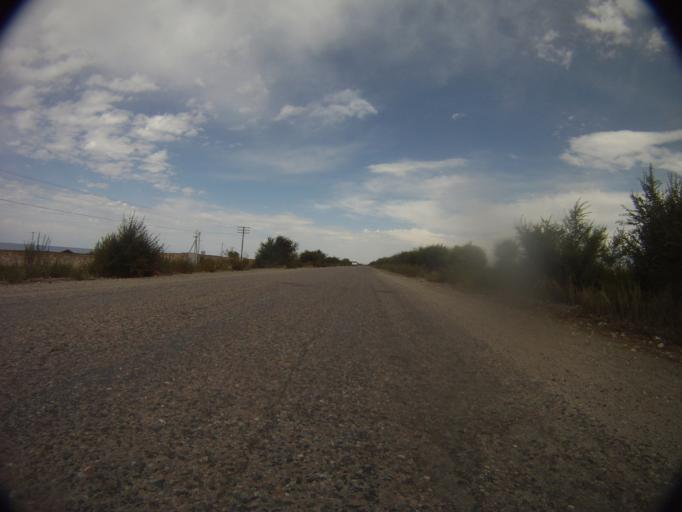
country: KG
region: Ysyk-Koel
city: Kadzhi-Say
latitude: 42.1740
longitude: 77.5434
